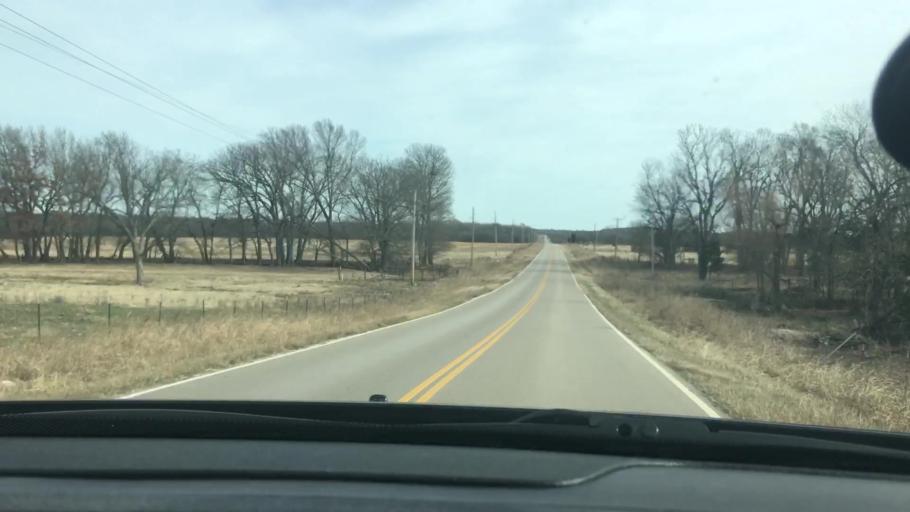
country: US
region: Oklahoma
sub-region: Murray County
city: Sulphur
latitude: 34.4050
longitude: -96.8776
